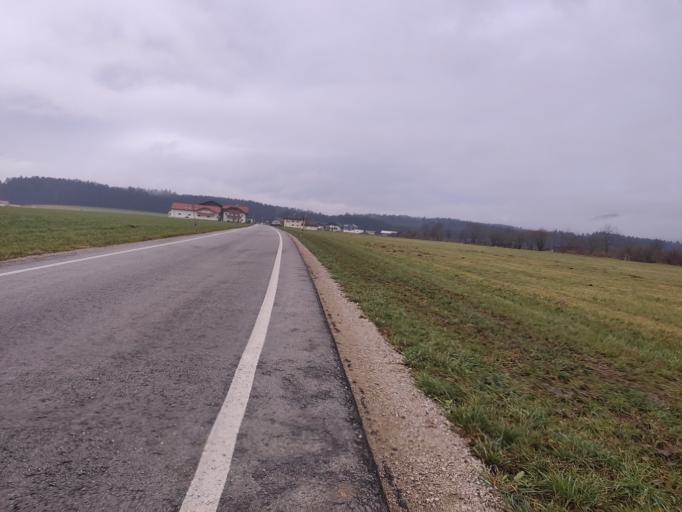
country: AT
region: Salzburg
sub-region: Politischer Bezirk Salzburg-Umgebung
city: Strasswalchen
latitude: 47.9757
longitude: 13.2412
